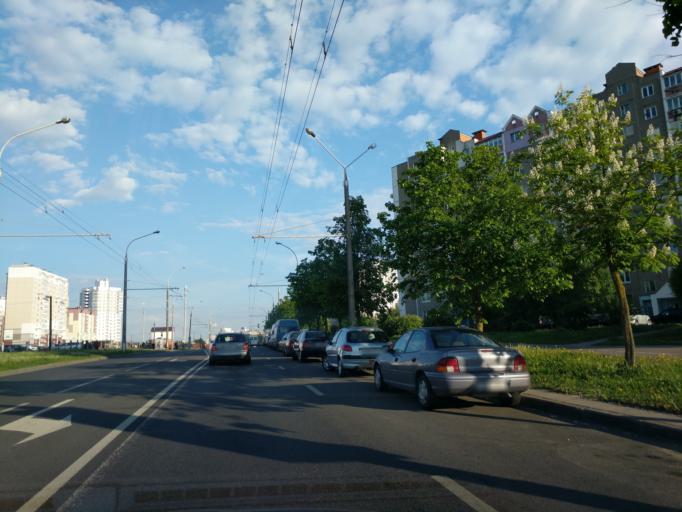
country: BY
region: Minsk
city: Novoye Medvezhino
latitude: 53.8905
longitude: 27.4402
